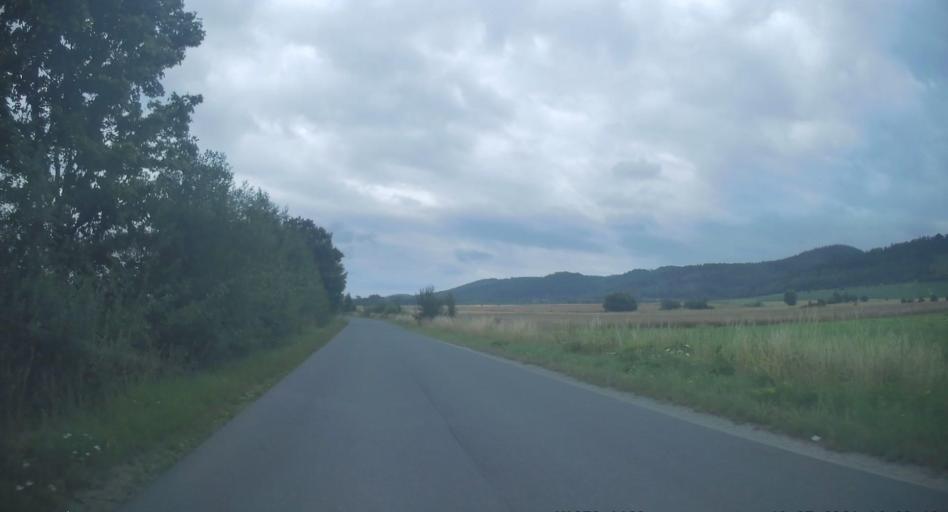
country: PL
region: Lower Silesian Voivodeship
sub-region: Powiat zabkowicki
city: Budzow
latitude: 50.5657
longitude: 16.6858
